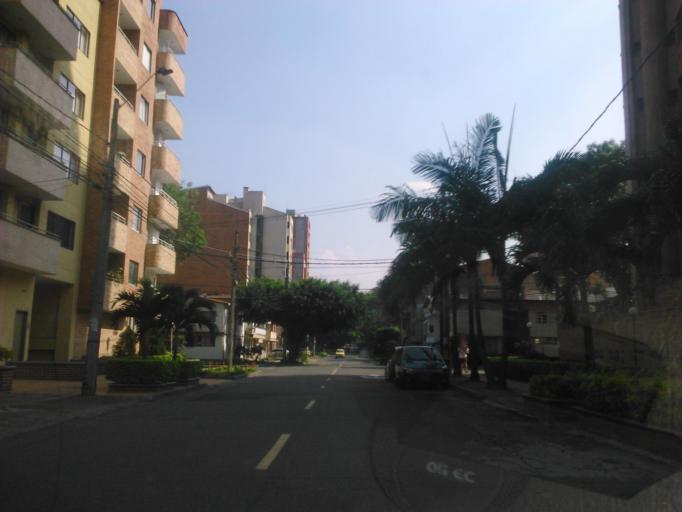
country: CO
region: Antioquia
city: Medellin
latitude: 6.2606
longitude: -75.5982
